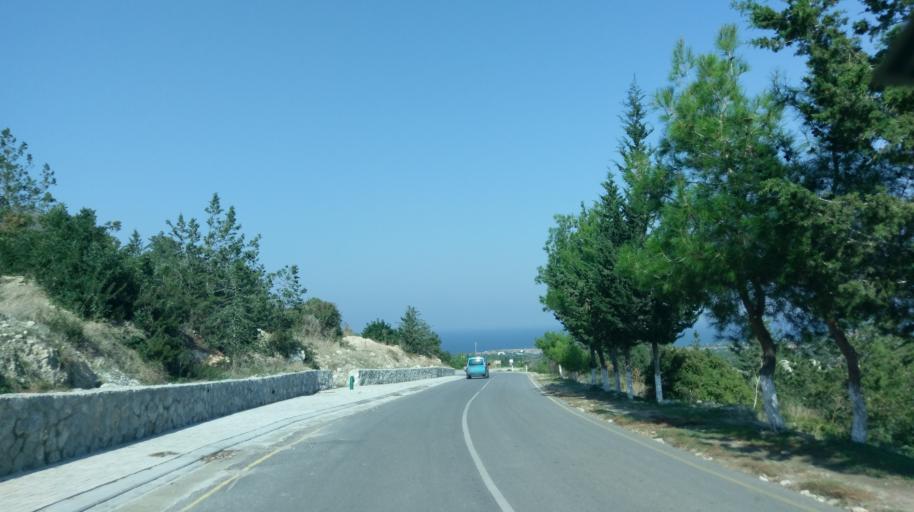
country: CY
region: Ammochostos
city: Lefkonoiko
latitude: 35.3860
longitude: 33.7517
